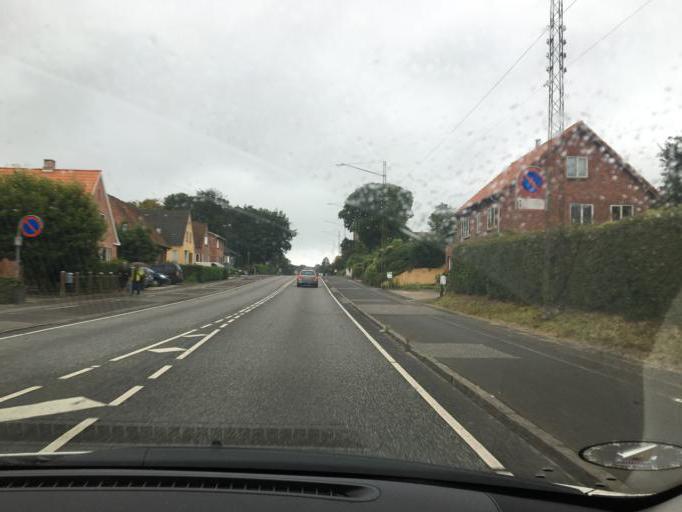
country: DK
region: South Denmark
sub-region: Middelfart Kommune
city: Middelfart
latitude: 55.5006
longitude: 9.7334
